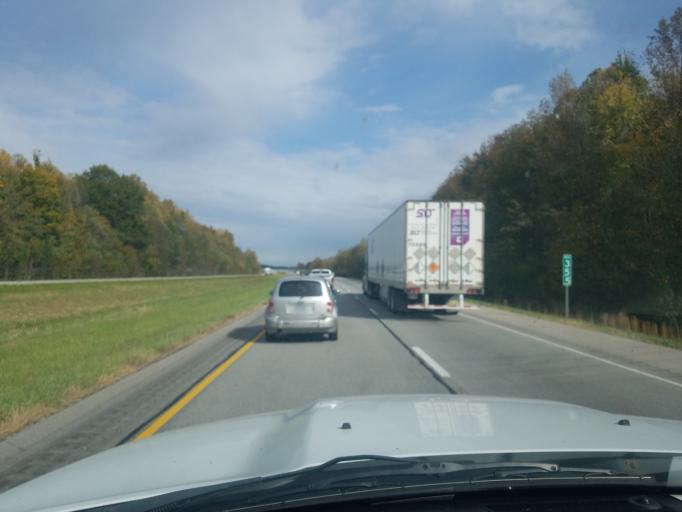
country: US
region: Indiana
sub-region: Warrick County
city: Chandler
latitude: 38.1850
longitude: -87.3625
